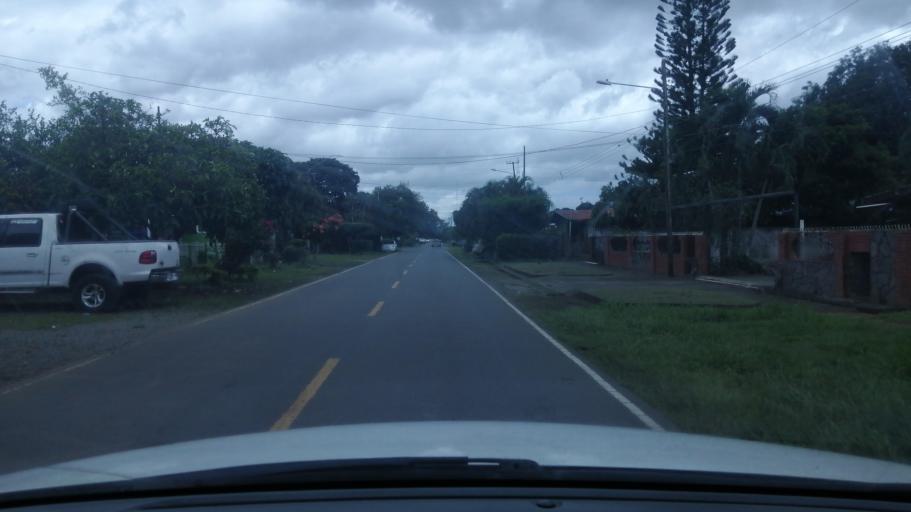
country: PA
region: Chiriqui
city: David
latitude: 8.4447
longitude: -82.4281
